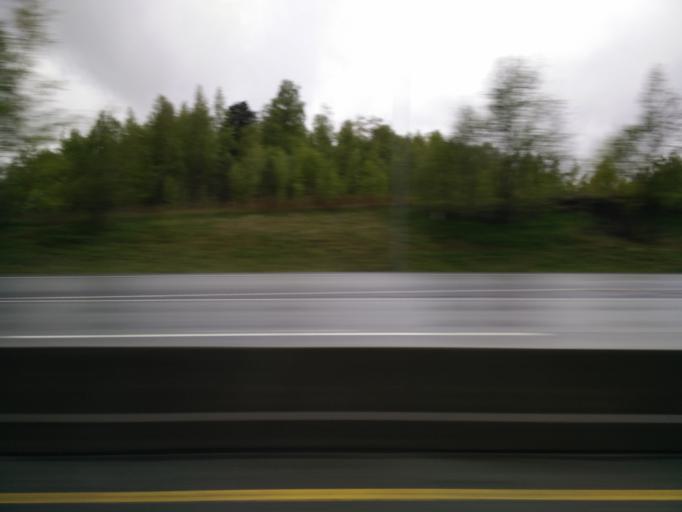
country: NO
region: Sor-Trondelag
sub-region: Malvik
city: Hommelvik
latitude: 63.4109
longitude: 10.8167
